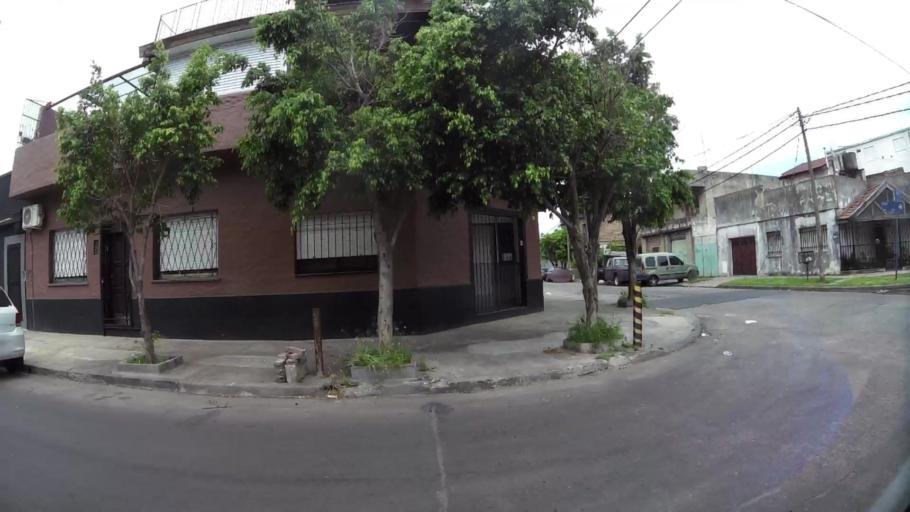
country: AR
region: Buenos Aires
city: San Justo
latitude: -34.6762
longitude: -58.5383
